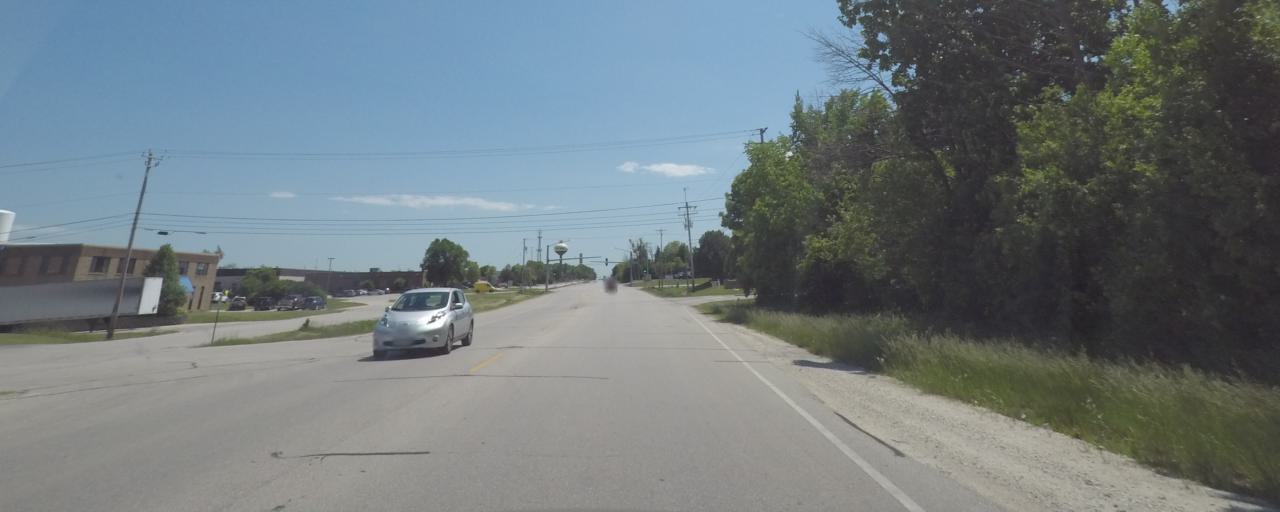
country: US
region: Wisconsin
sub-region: Waukesha County
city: New Berlin
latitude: 43.0039
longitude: -88.1275
